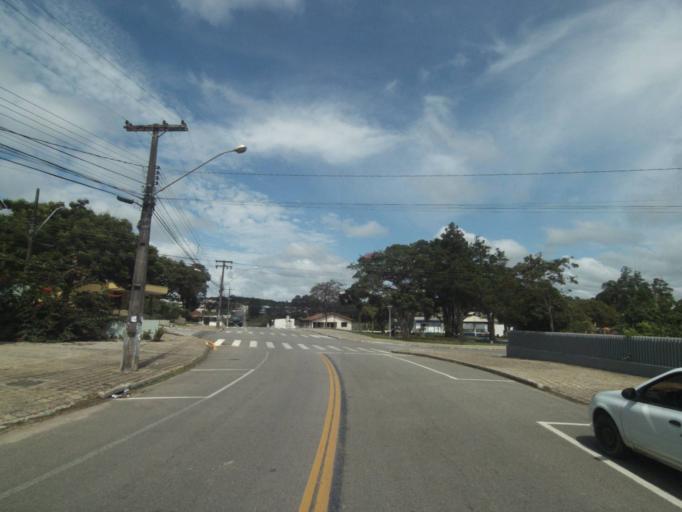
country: BR
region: Parana
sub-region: Campina Grande Do Sul
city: Campina Grande do Sul
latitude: -25.3066
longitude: -49.0529
